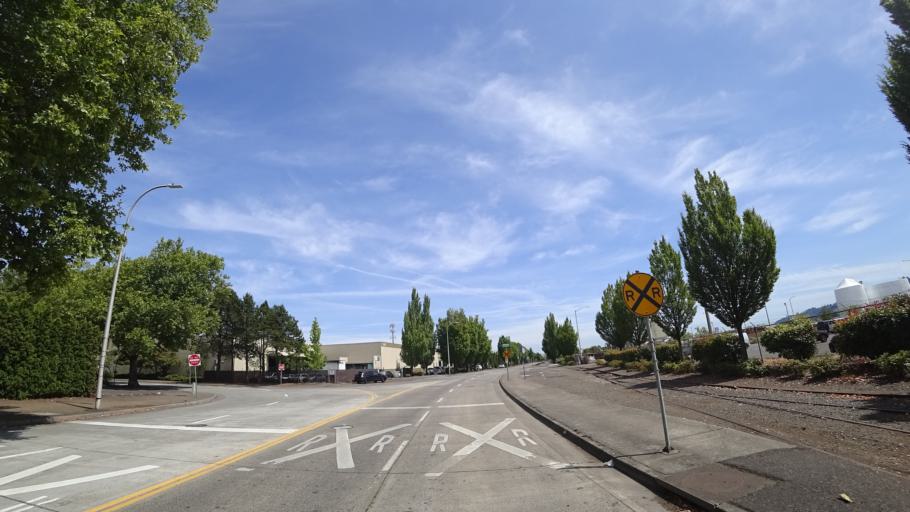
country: US
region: Oregon
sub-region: Multnomah County
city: Portland
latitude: 45.5625
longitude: -122.7161
